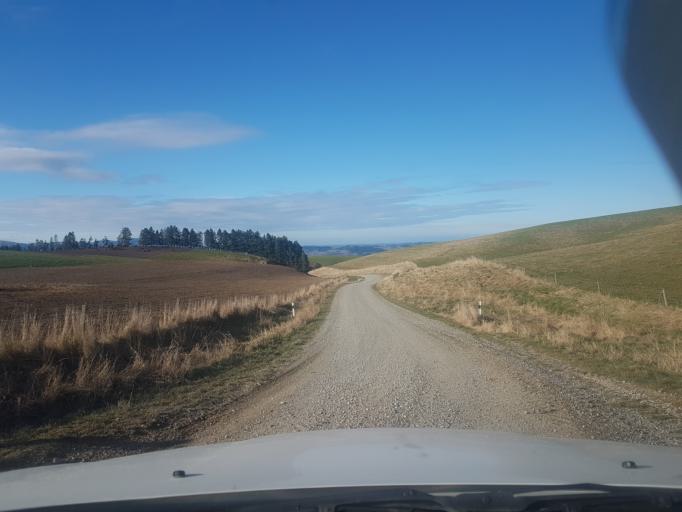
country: NZ
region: Canterbury
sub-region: Timaru District
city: Pleasant Point
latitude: -44.1665
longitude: 170.8928
